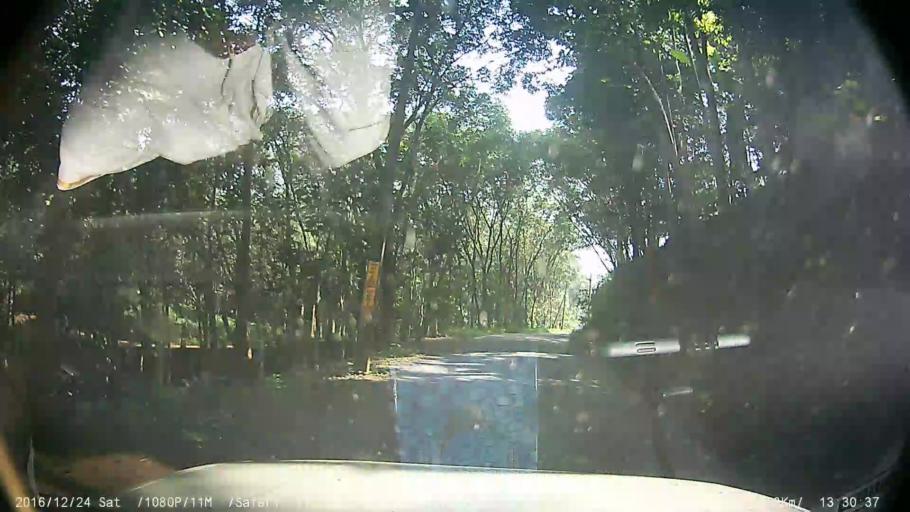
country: IN
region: Kerala
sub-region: Kottayam
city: Palackattumala
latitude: 9.8468
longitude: 76.7030
